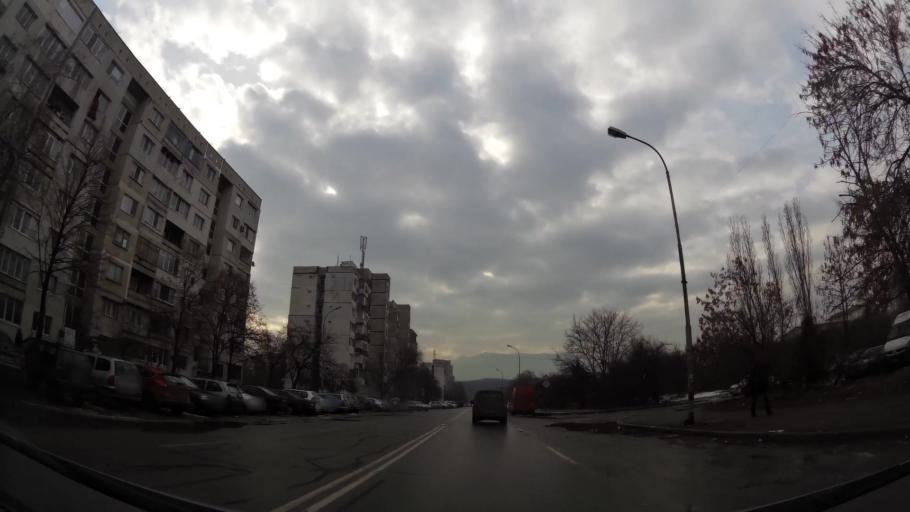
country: BG
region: Sofia-Capital
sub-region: Stolichna Obshtina
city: Sofia
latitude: 42.7139
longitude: 23.2583
